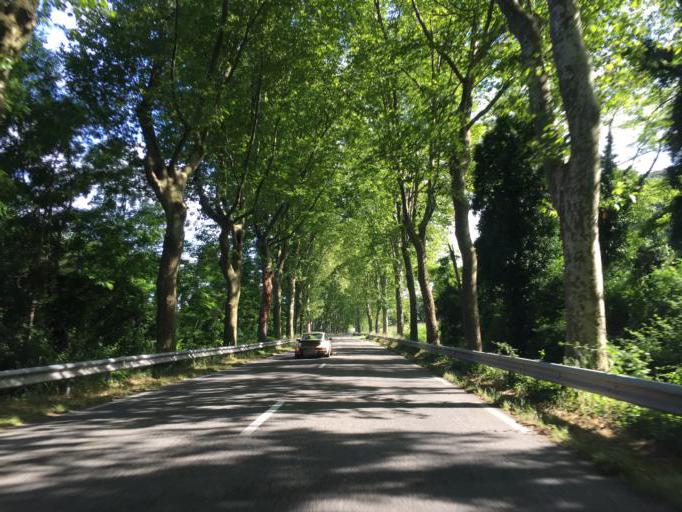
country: FR
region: Rhone-Alpes
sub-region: Departement de la Drome
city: Saulce-sur-Rhone
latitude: 44.6874
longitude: 4.7720
